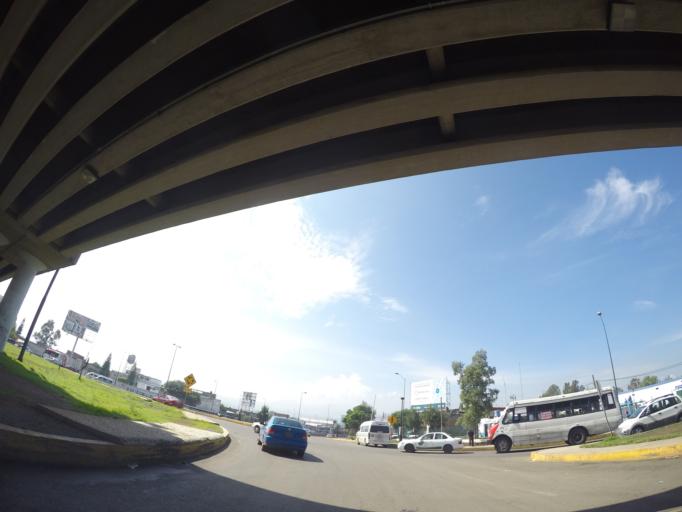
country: MX
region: Michoacan
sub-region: Morelia
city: San Antonio
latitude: 19.7001
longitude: -101.2438
